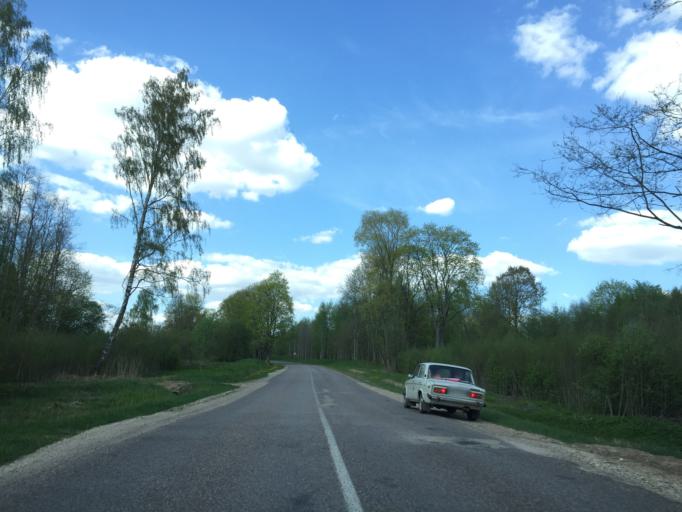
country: LV
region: Limbazu Rajons
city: Limbazi
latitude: 57.4757
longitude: 24.7108
